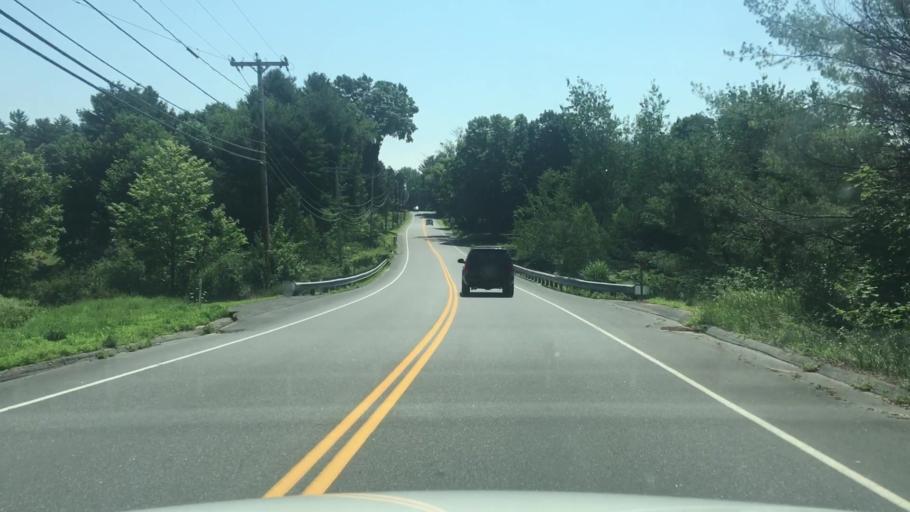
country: US
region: Maine
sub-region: Cumberland County
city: Cumberland Center
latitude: 43.8016
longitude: -70.2686
